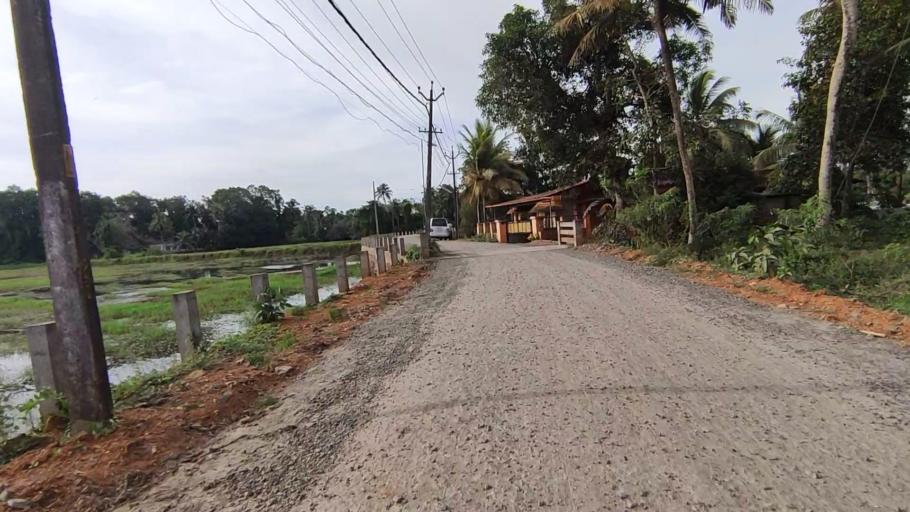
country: IN
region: Kerala
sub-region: Kottayam
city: Kottayam
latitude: 9.5750
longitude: 76.4922
